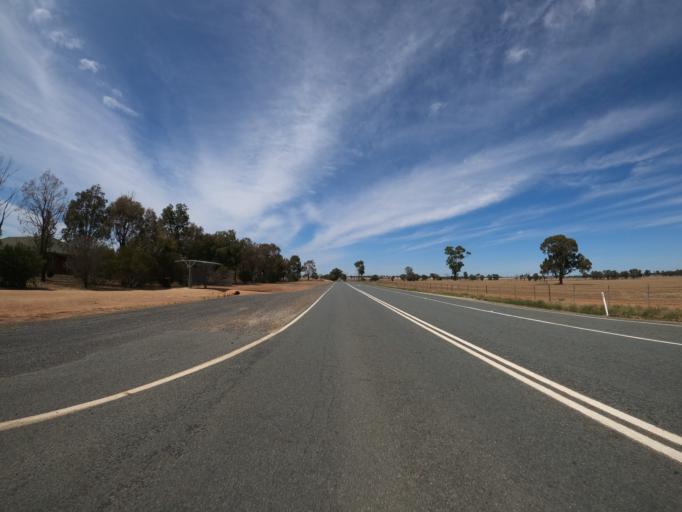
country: AU
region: Victoria
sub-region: Moira
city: Yarrawonga
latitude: -36.0486
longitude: 145.9955
